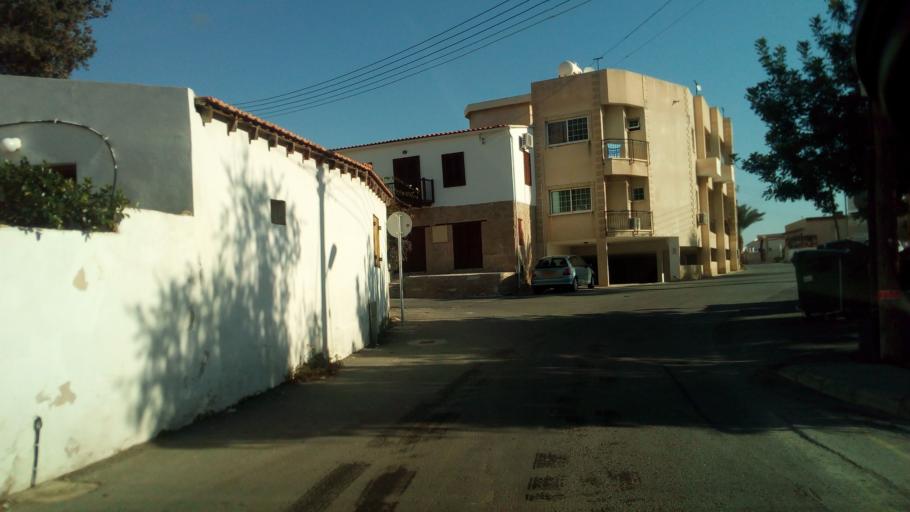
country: CY
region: Larnaka
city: Voroklini
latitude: 34.9881
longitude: 33.6509
